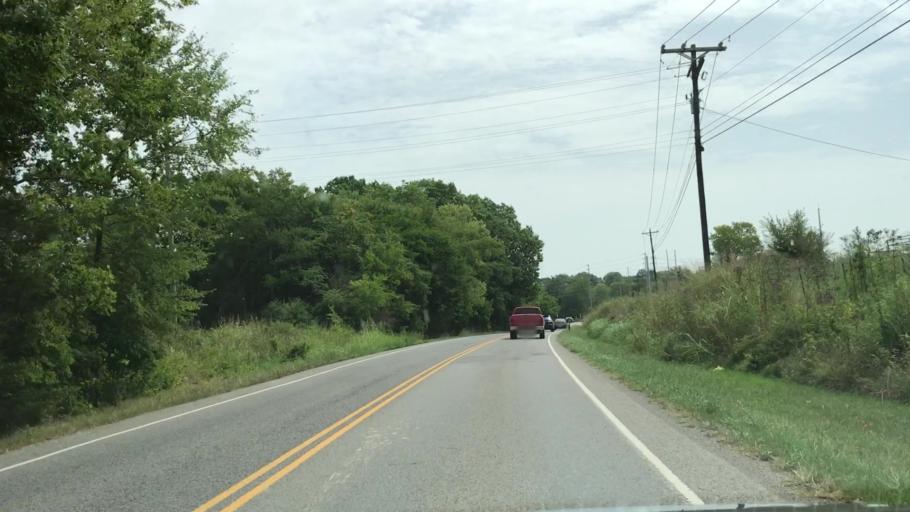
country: US
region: Tennessee
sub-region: Williamson County
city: Nolensville
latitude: 35.9402
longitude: -86.6779
